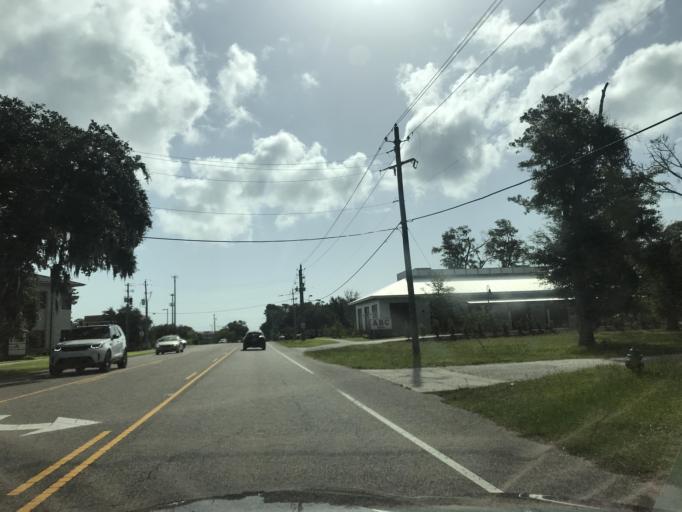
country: US
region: North Carolina
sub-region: New Hanover County
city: Seagate
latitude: 34.2203
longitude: -77.8238
